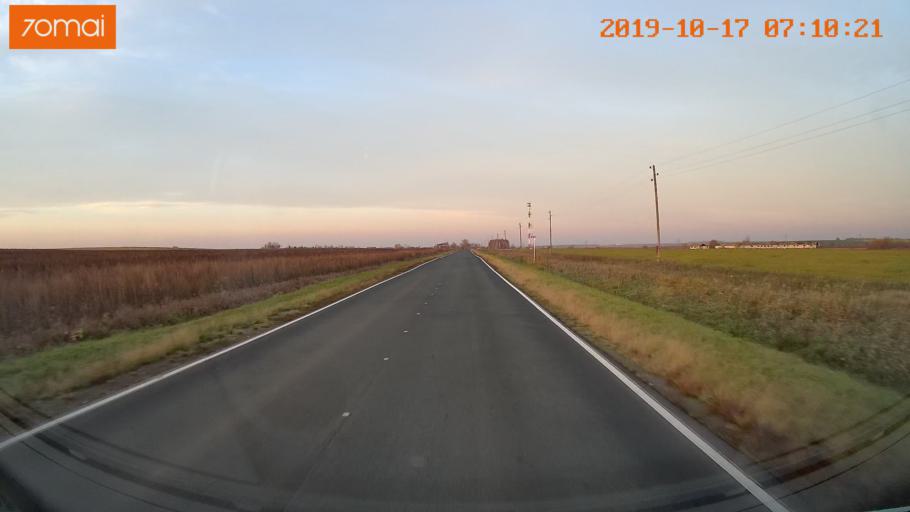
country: RU
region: Vladimir
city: Suzdal'
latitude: 56.4123
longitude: 40.3633
